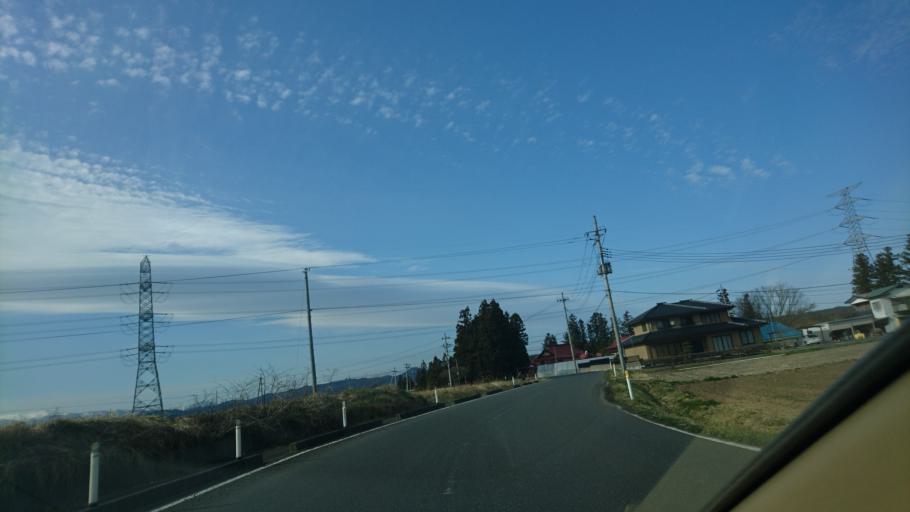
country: JP
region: Iwate
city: Ichinoseki
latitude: 38.8114
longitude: 141.0269
